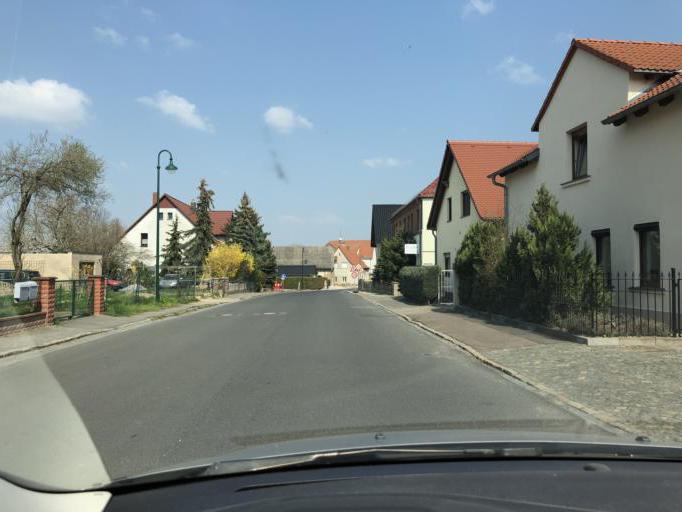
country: DE
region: Saxony
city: Rackwitz
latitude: 51.4244
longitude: 12.3816
